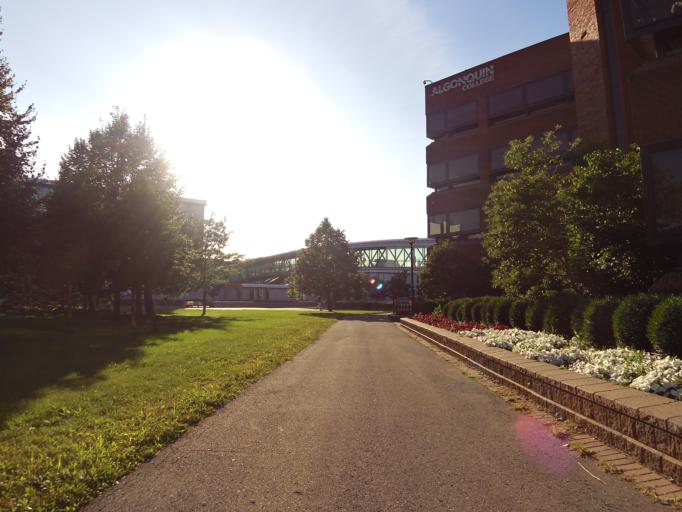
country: CA
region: Ontario
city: Bells Corners
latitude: 45.3476
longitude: -75.7589
